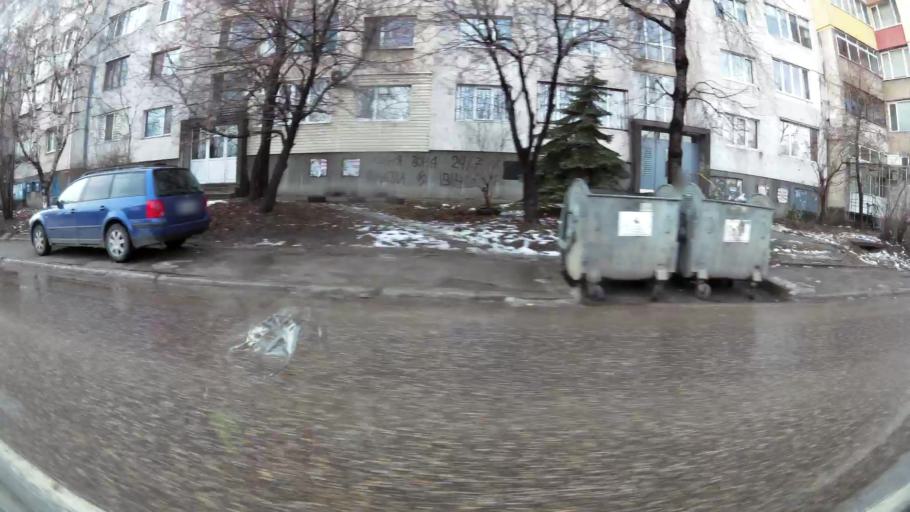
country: BG
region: Sofia-Capital
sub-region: Stolichna Obshtina
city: Sofia
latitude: 42.7181
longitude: 23.2727
